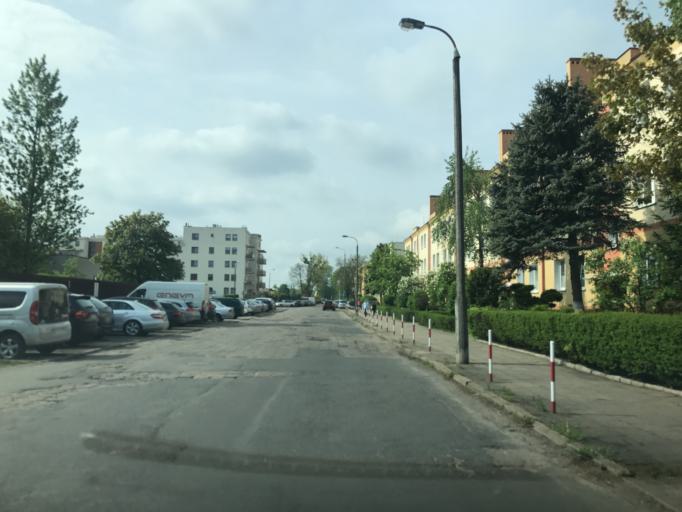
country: PL
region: Kujawsko-Pomorskie
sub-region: Bydgoszcz
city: Bydgoszcz
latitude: 53.1432
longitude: 18.0115
